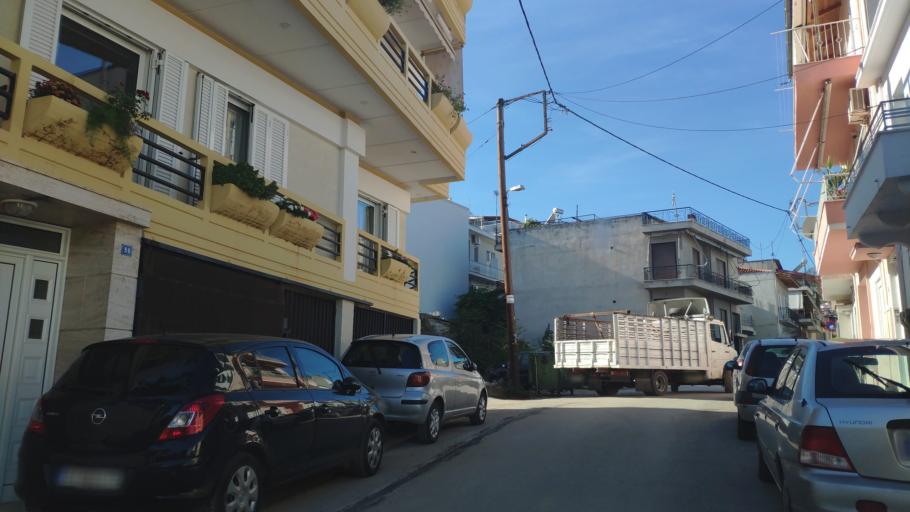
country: GR
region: Central Greece
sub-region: Nomos Voiotias
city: Livadeia
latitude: 38.4363
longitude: 22.8779
